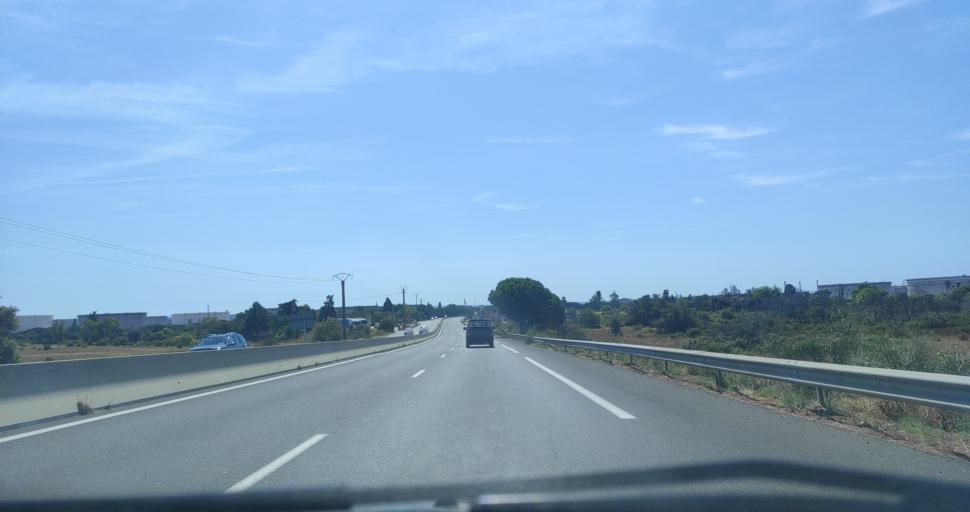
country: FR
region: Provence-Alpes-Cote d'Azur
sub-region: Departement des Bouches-du-Rhone
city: Fos-sur-Mer
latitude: 43.4724
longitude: 4.9045
